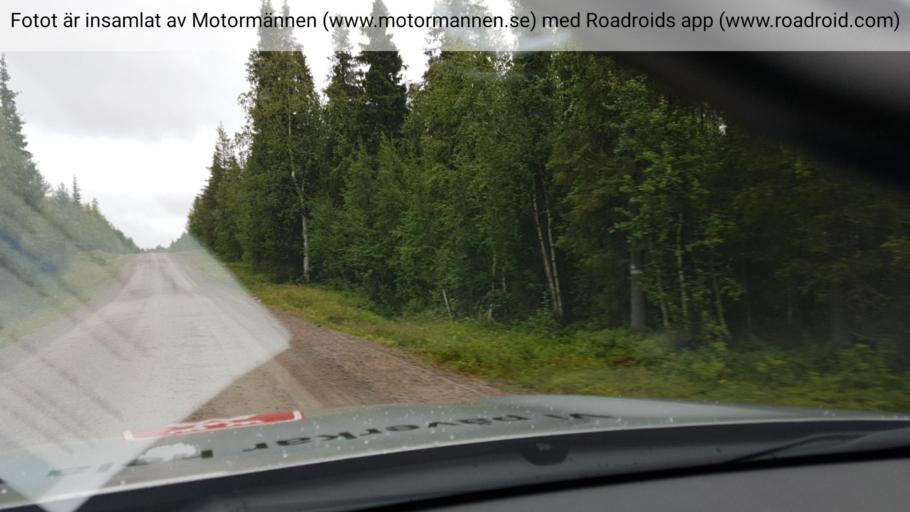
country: SE
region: Norrbotten
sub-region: Gallivare Kommun
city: Gaellivare
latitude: 66.6986
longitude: 20.3948
